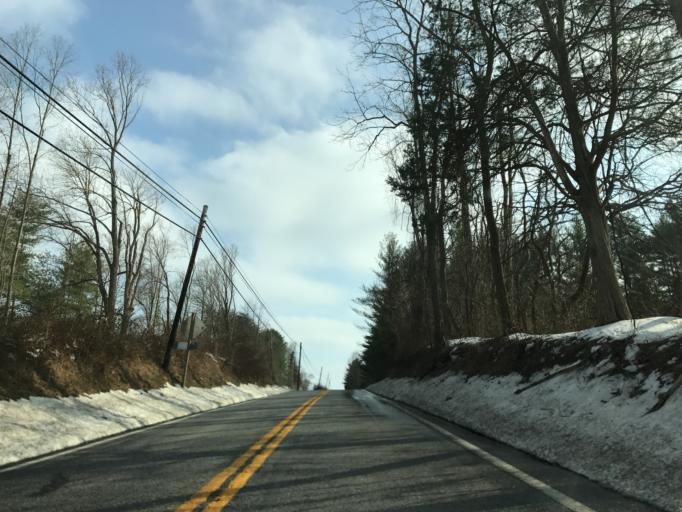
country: US
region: Maryland
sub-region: Harford County
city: South Bel Air
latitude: 39.5954
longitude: -76.2594
